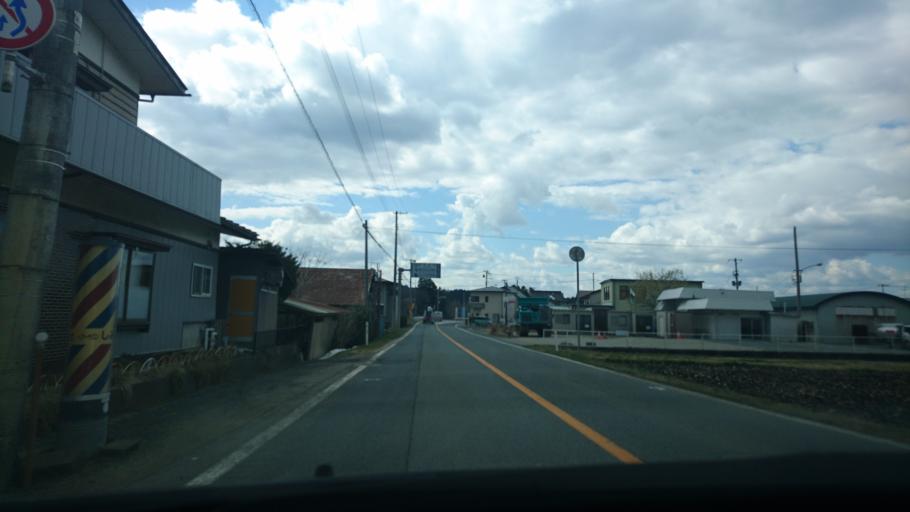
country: JP
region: Iwate
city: Hanamaki
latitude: 39.3632
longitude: 141.2607
